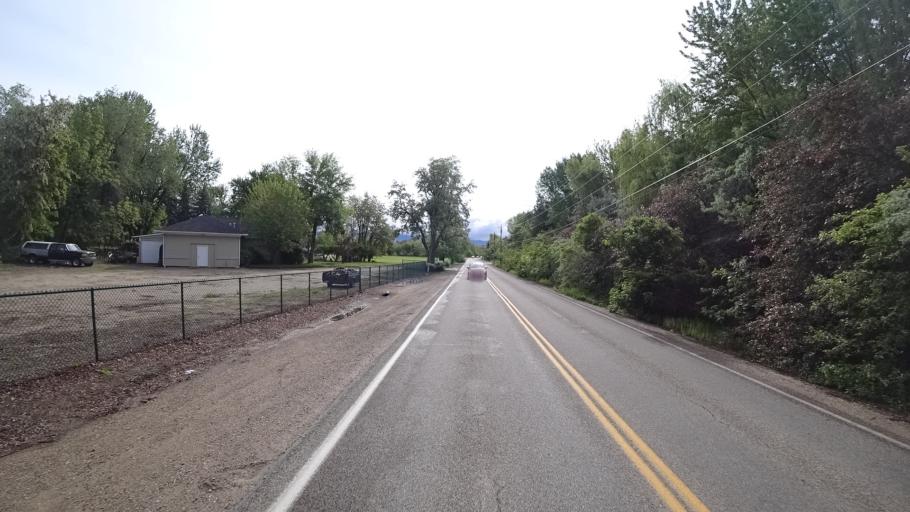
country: US
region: Idaho
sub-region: Ada County
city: Eagle
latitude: 43.7208
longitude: -116.3433
